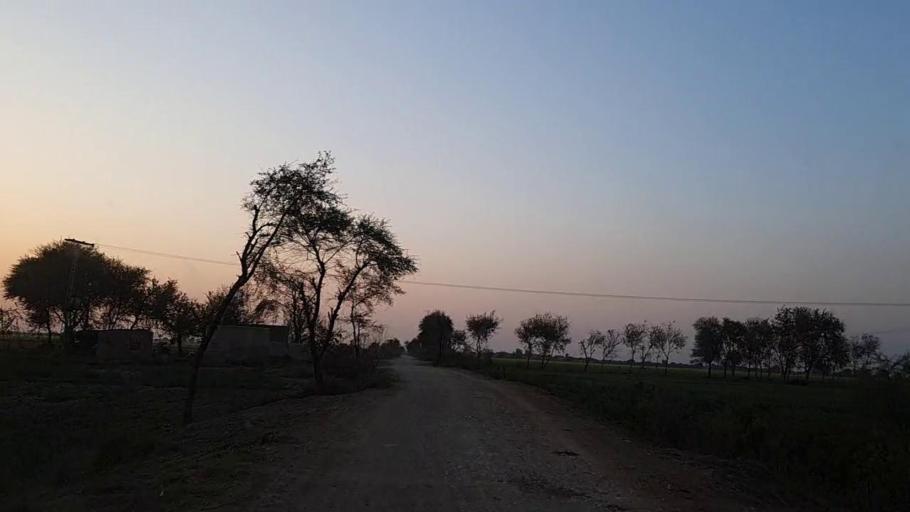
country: PK
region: Sindh
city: Hala
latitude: 25.9315
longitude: 68.4729
